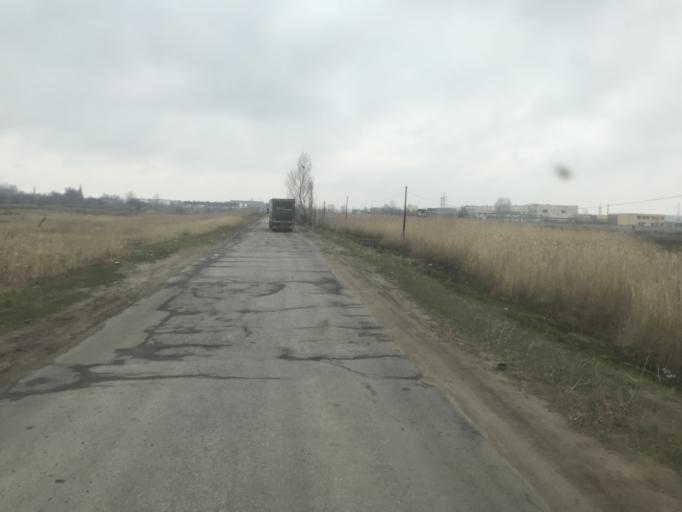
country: RU
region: Volgograd
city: Svetlyy Yar
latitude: 48.5198
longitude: 44.6250
